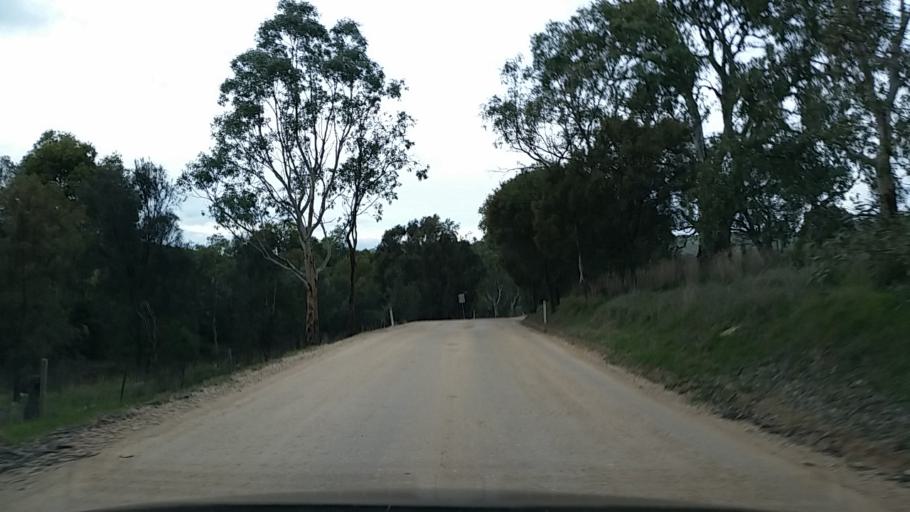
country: AU
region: South Australia
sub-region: Mount Barker
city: Nairne
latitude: -34.9544
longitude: 139.0125
